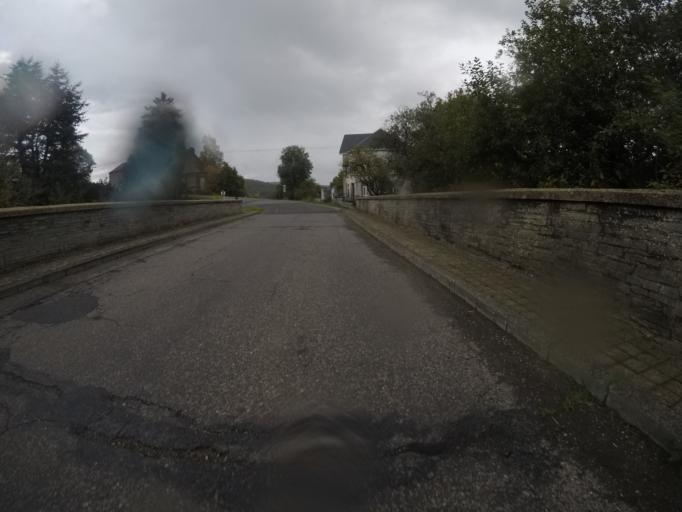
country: BE
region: Wallonia
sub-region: Province du Luxembourg
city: Fauvillers
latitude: 49.8757
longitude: 5.6767
